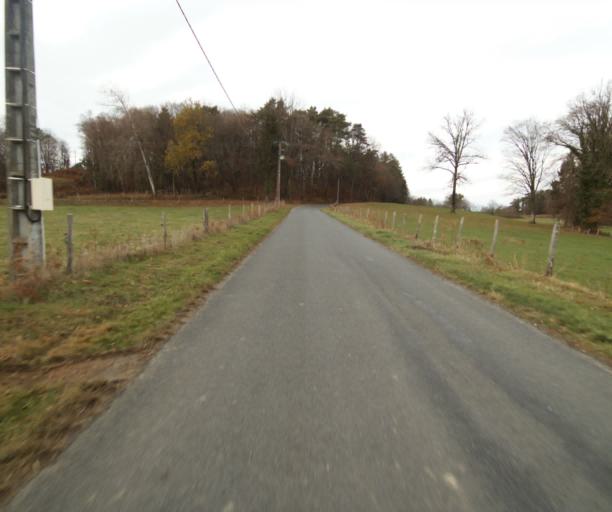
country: FR
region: Limousin
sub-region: Departement de la Correze
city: Chameyrat
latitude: 45.2515
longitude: 1.6817
